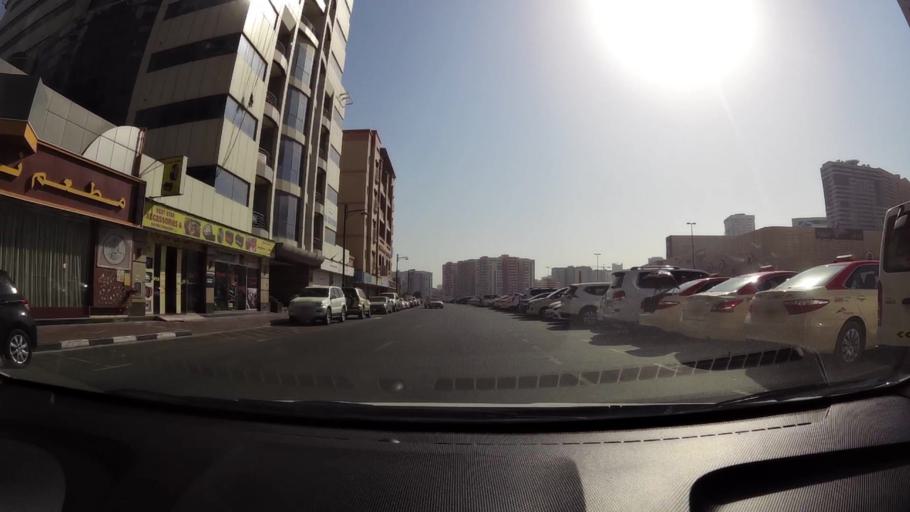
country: AE
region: Ash Shariqah
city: Sharjah
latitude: 25.2973
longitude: 55.3779
